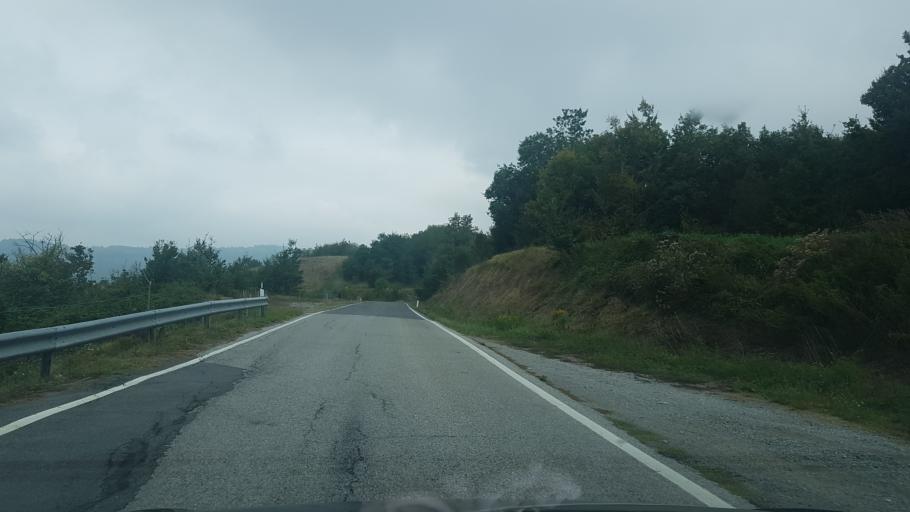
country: IT
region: Piedmont
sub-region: Provincia di Cuneo
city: Paroldo
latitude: 44.4323
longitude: 8.0832
